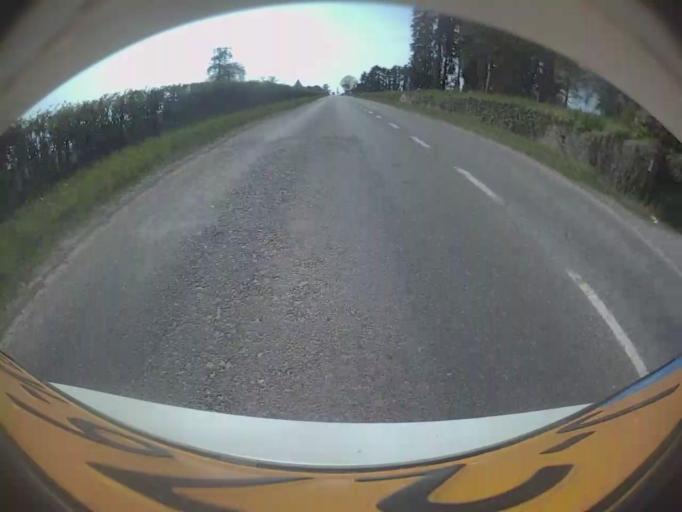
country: BE
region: Wallonia
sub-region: Province de Namur
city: Dinant
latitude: 50.2583
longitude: 4.9862
